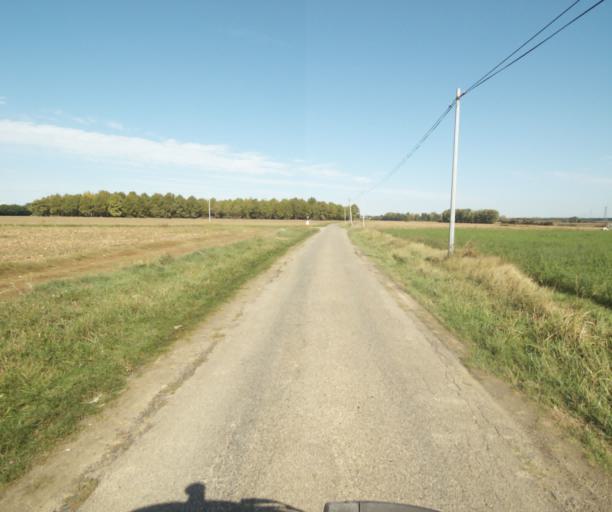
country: FR
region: Midi-Pyrenees
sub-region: Departement du Tarn-et-Garonne
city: Verdun-sur-Garonne
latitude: 43.8777
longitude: 1.2350
